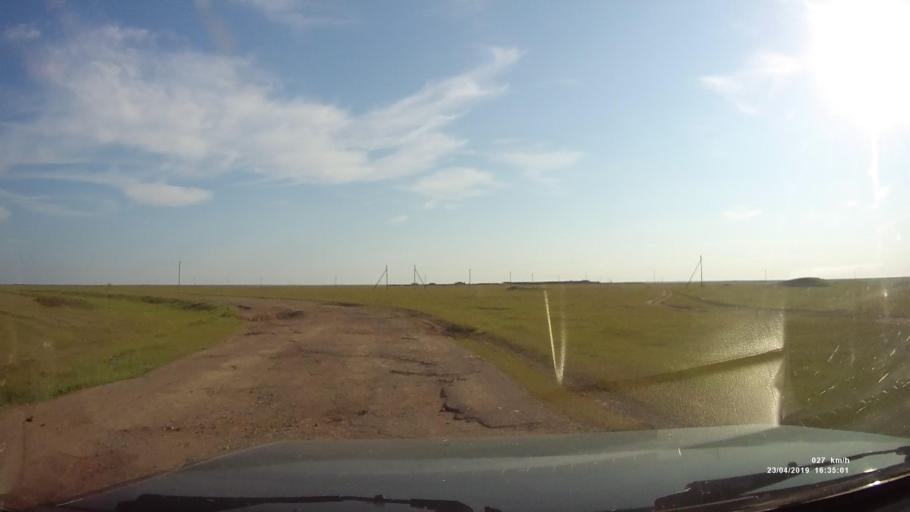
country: RU
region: Kalmykiya
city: Priyutnoye
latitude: 46.3323
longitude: 43.1364
